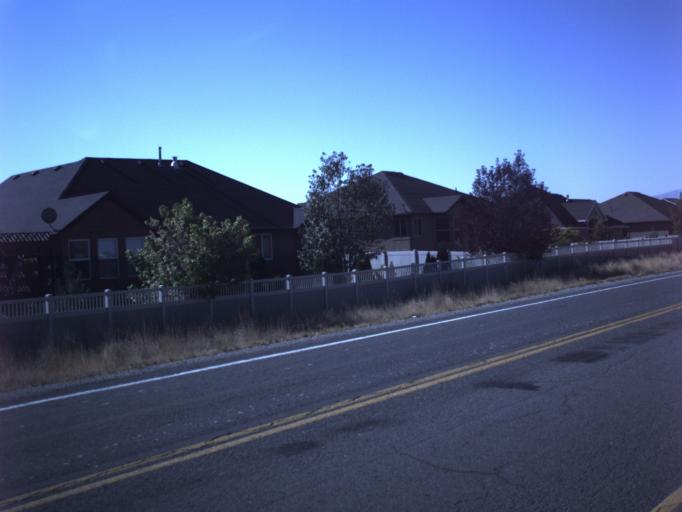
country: US
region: Utah
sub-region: Tooele County
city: Stansbury park
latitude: 40.6477
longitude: -112.3016
